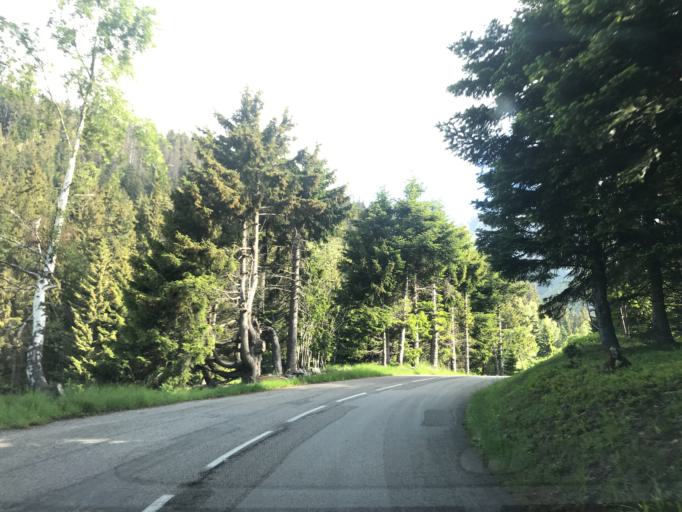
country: FR
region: Rhone-Alpes
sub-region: Departement de la Savoie
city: Modane
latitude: 45.2110
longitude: 6.6475
